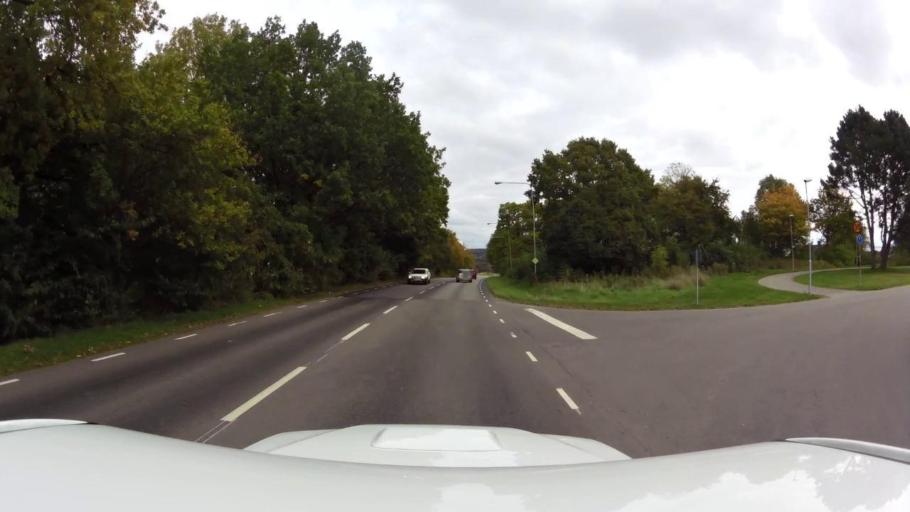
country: SE
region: OEstergoetland
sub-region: Linkopings Kommun
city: Berg
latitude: 58.4922
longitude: 15.5284
